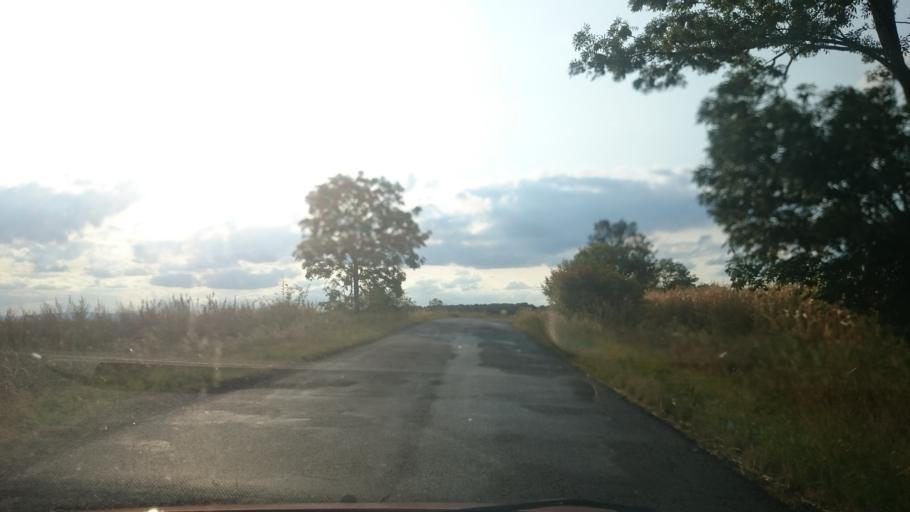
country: PL
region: Opole Voivodeship
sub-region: Powiat nyski
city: Otmuchow
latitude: 50.5087
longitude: 17.1516
